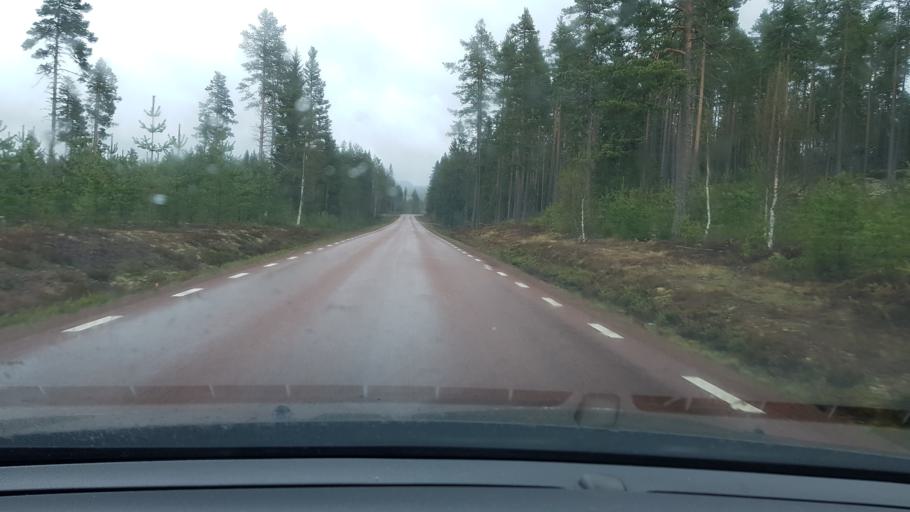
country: SE
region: Dalarna
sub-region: Alvdalens Kommun
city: AElvdalen
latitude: 61.1198
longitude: 14.0865
